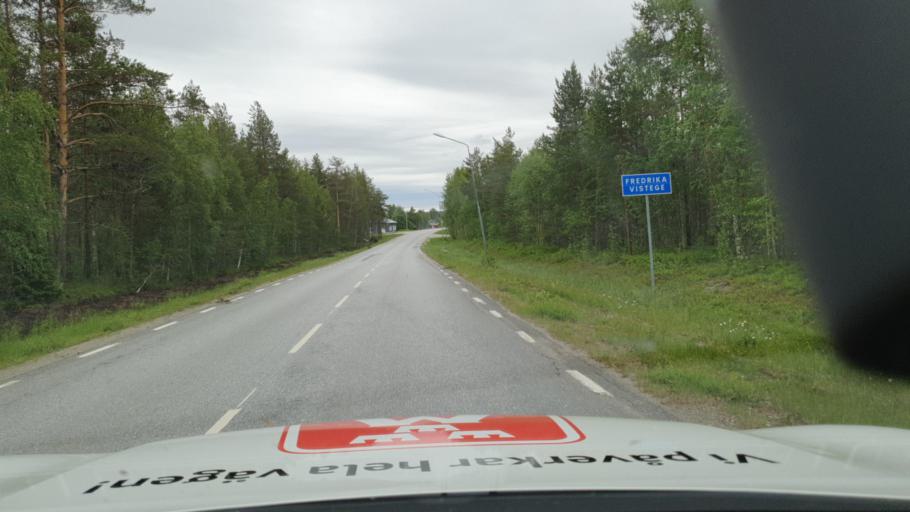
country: SE
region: Vaesterbotten
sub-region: Lycksele Kommun
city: Lycksele
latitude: 64.0843
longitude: 18.3985
